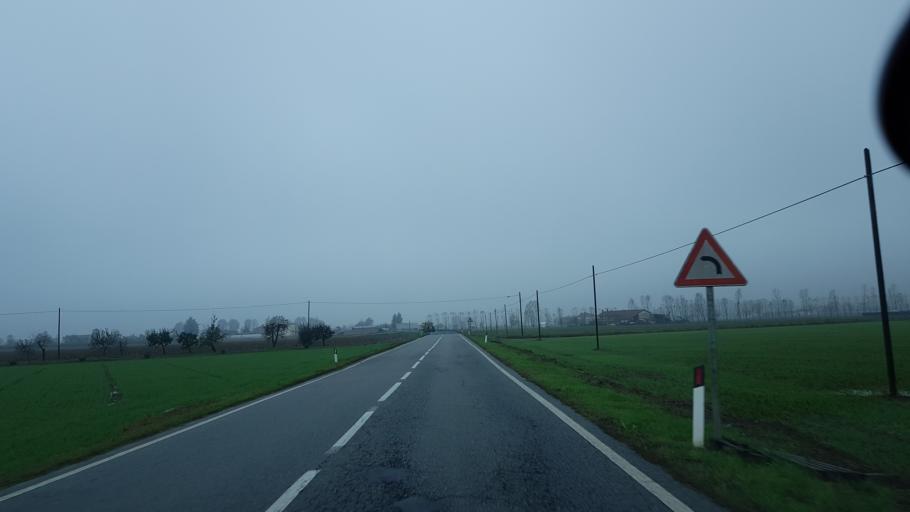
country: IT
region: Piedmont
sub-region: Provincia di Cuneo
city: Genola
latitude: 44.5577
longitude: 7.6529
